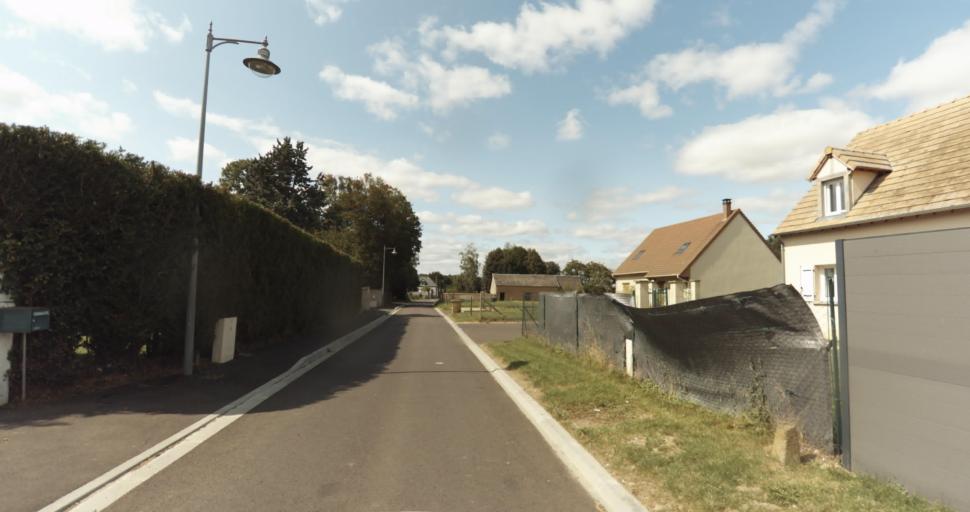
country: FR
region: Haute-Normandie
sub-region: Departement de l'Eure
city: Nonancourt
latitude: 48.8422
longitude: 1.1642
